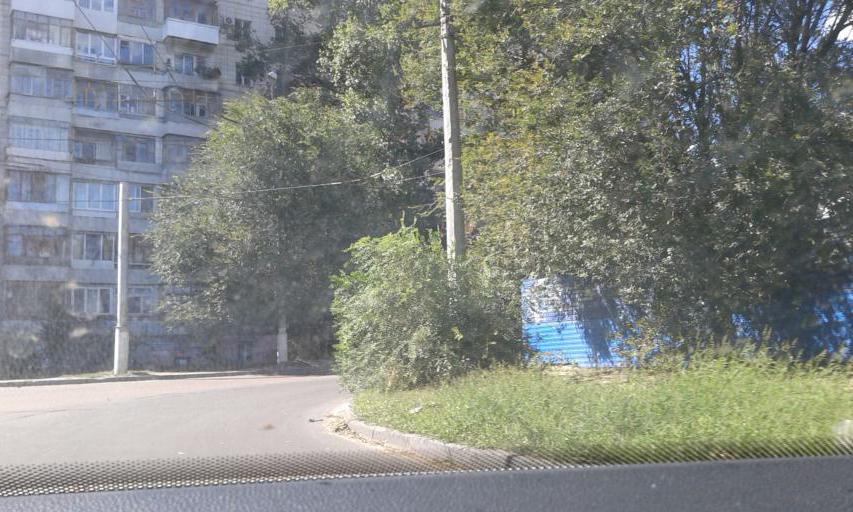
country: RU
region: Volgograd
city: Volgograd
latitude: 48.6789
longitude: 44.4763
